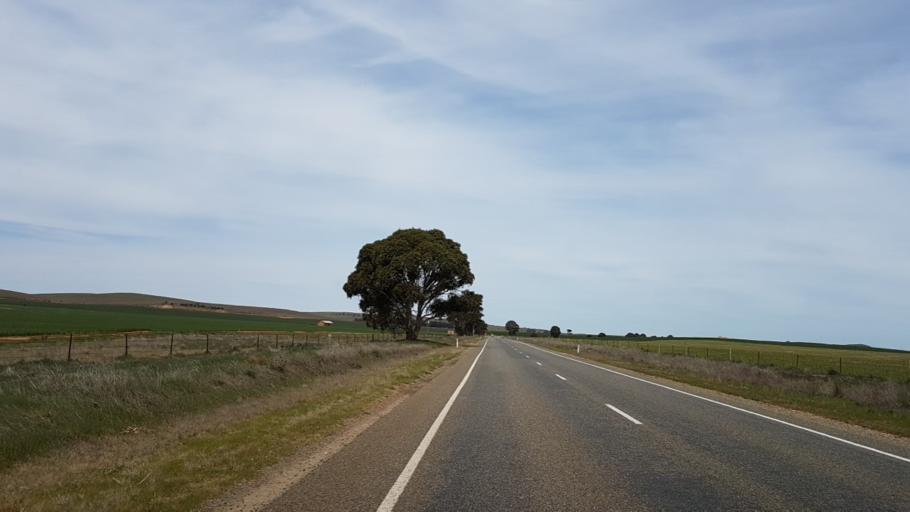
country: AU
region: South Australia
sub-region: Northern Areas
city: Jamestown
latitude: -33.0836
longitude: 138.6178
